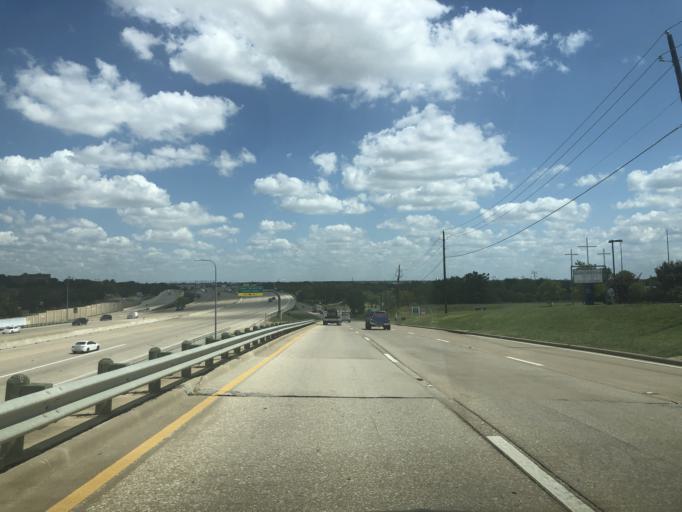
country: US
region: Texas
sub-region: Dallas County
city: Grand Prairie
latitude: 32.7673
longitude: -97.0279
